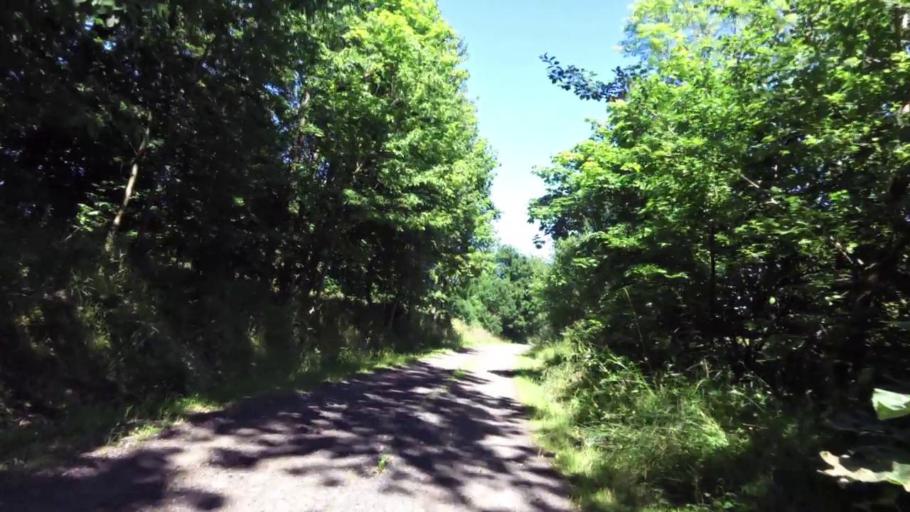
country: PL
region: West Pomeranian Voivodeship
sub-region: Powiat kolobrzeski
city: Goscino
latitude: 54.0437
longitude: 15.7246
